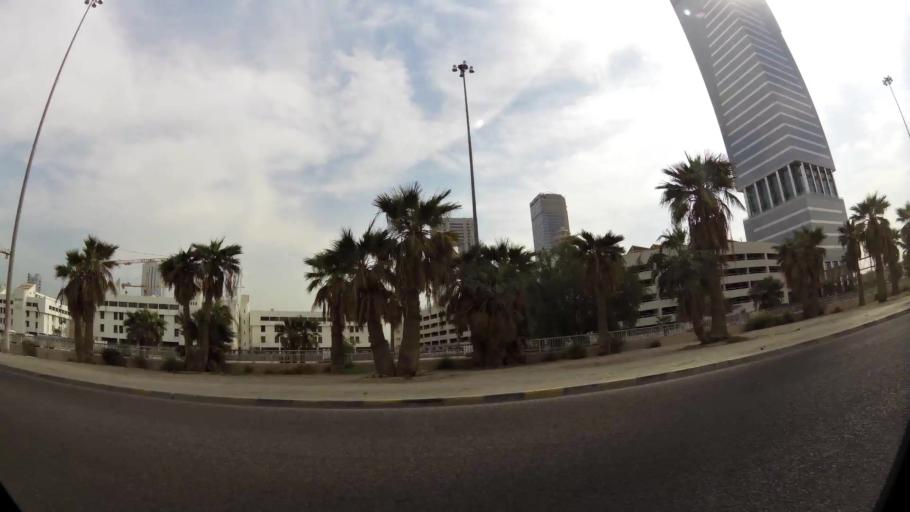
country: KW
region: Al Asimah
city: Kuwait City
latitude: 29.3632
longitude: 47.9743
